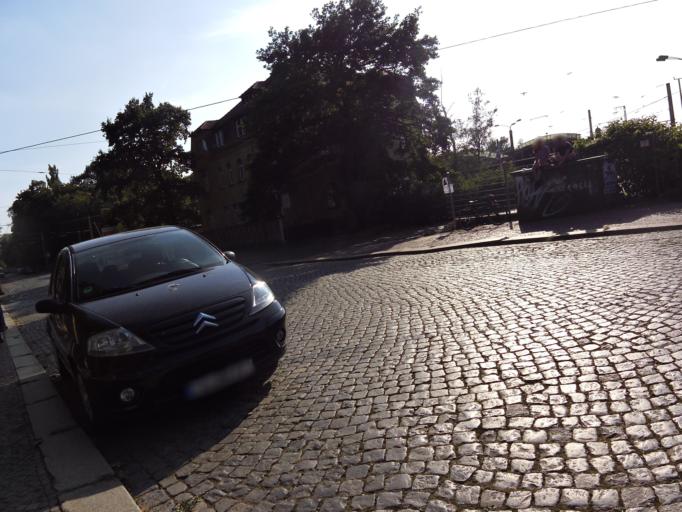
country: DE
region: Saxony
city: Leipzig
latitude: 51.3566
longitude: 12.3156
